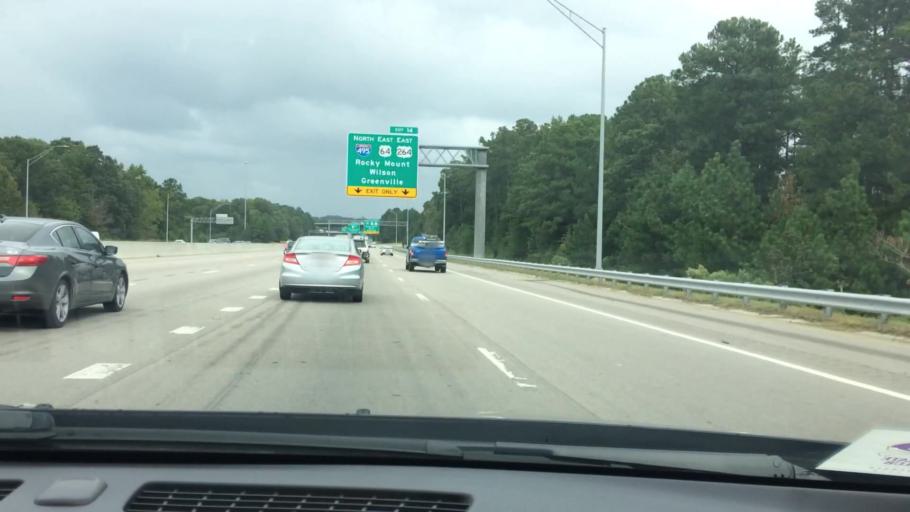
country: US
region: North Carolina
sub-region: Wake County
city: Raleigh
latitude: 35.7735
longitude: -78.5737
